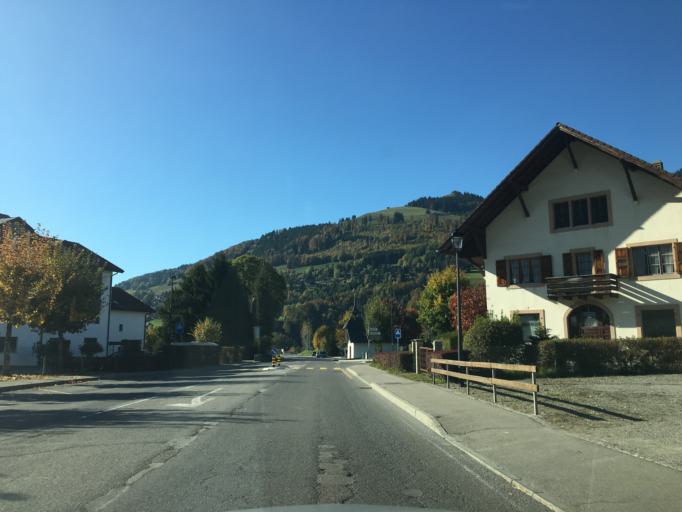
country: CH
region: Fribourg
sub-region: Gruyere District
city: Charmey
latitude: 46.6203
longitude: 7.1599
